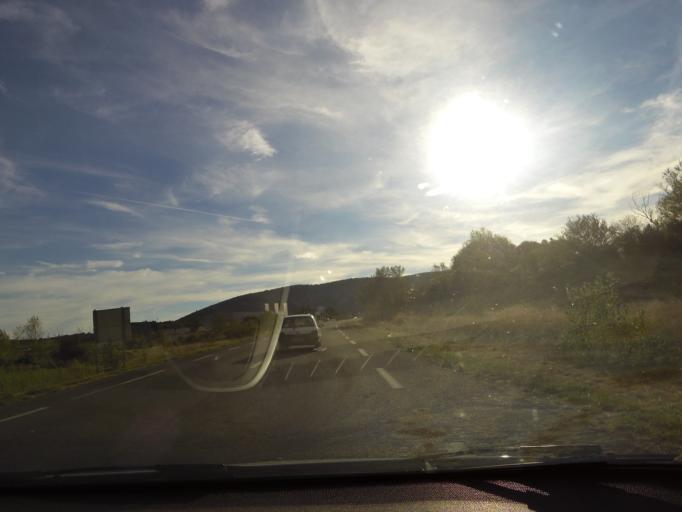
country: FR
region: Languedoc-Roussillon
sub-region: Departement du Gard
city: Quissac
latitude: 43.9014
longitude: 3.9962
